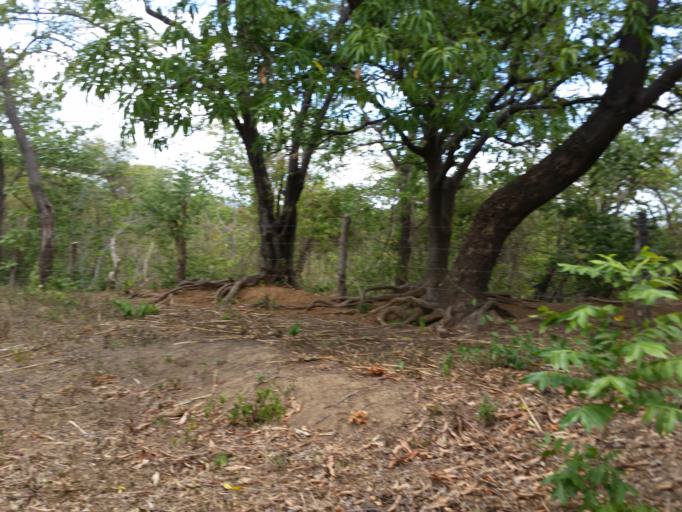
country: NI
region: Managua
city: Carlos Fonseca Amador
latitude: 11.9608
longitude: -86.4340
